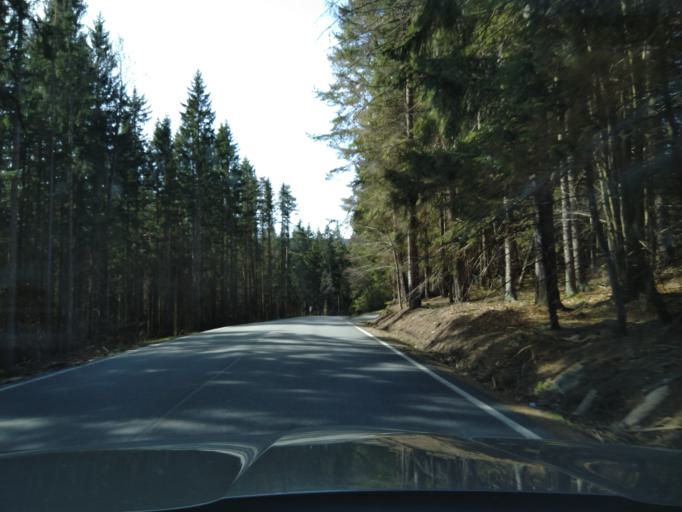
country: CZ
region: Jihocesky
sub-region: Okres Prachatice
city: Stachy
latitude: 49.0808
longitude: 13.6390
